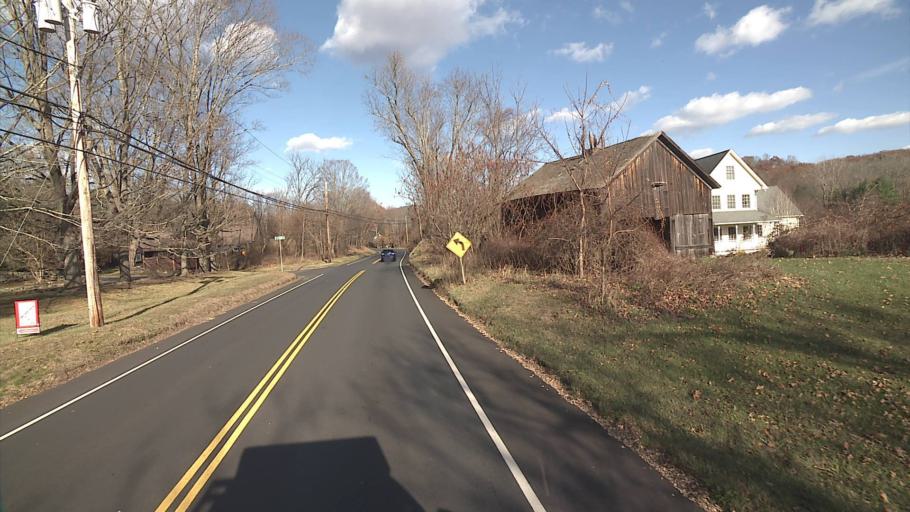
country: US
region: Connecticut
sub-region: Fairfield County
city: Bethel
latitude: 41.3318
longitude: -73.4197
